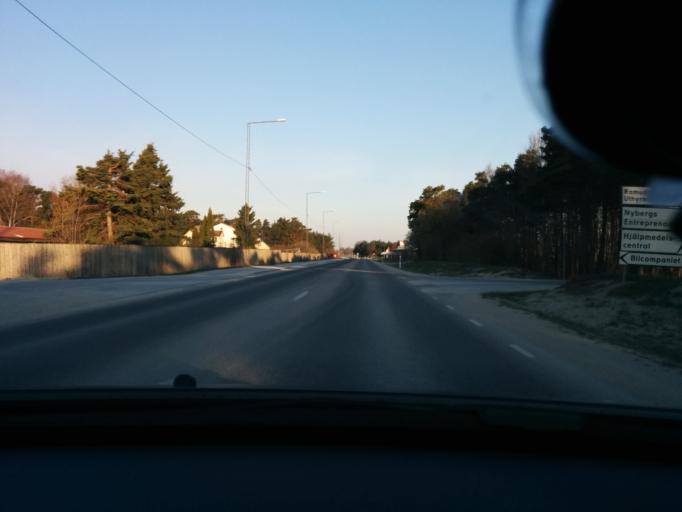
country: SE
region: Gotland
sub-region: Gotland
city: Visby
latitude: 57.6306
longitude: 18.3411
